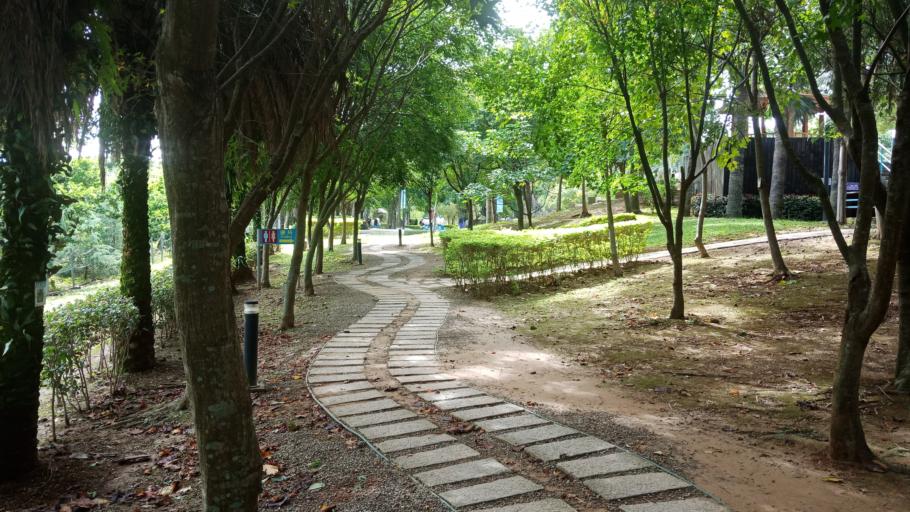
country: TW
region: Taiwan
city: Daxi
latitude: 24.8449
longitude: 121.2351
